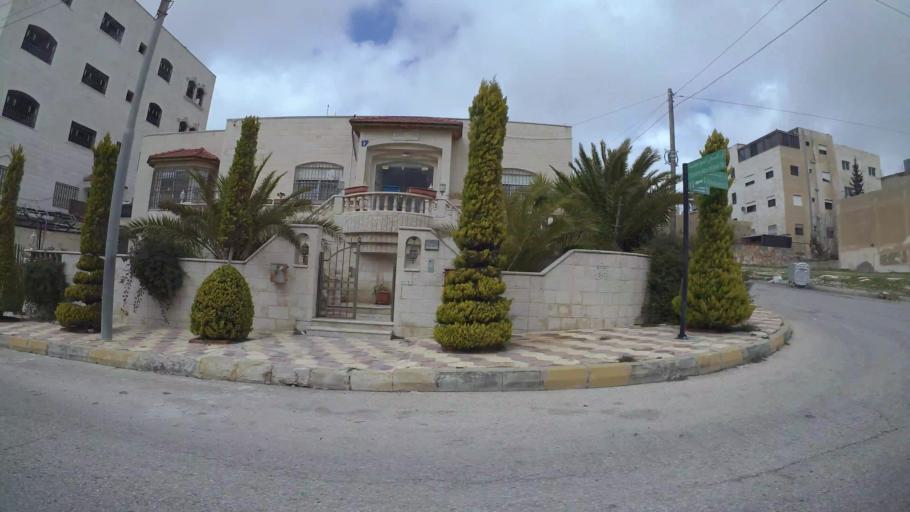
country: JO
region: Amman
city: Al Jubayhah
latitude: 32.0639
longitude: 35.8811
